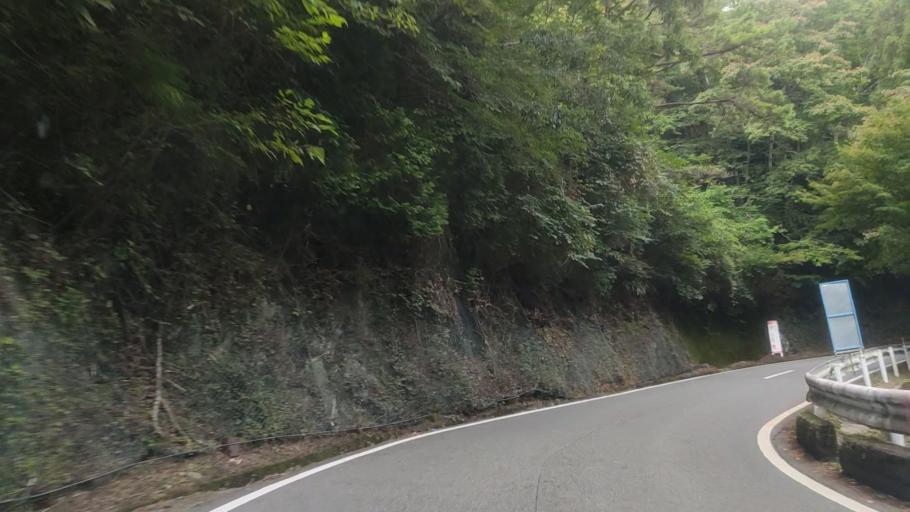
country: JP
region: Wakayama
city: Koya
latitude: 34.2170
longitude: 135.5691
